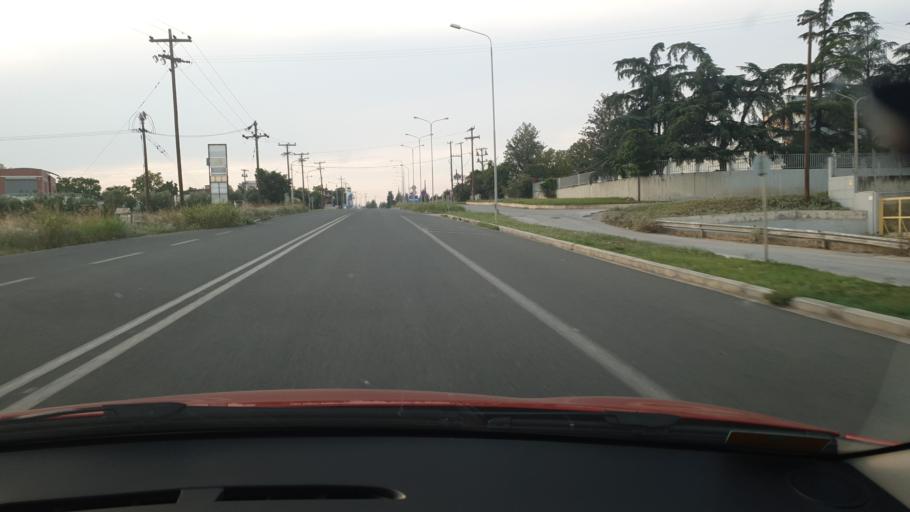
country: GR
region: Central Macedonia
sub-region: Nomos Thessalonikis
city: Thermi
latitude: 40.5303
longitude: 23.0427
